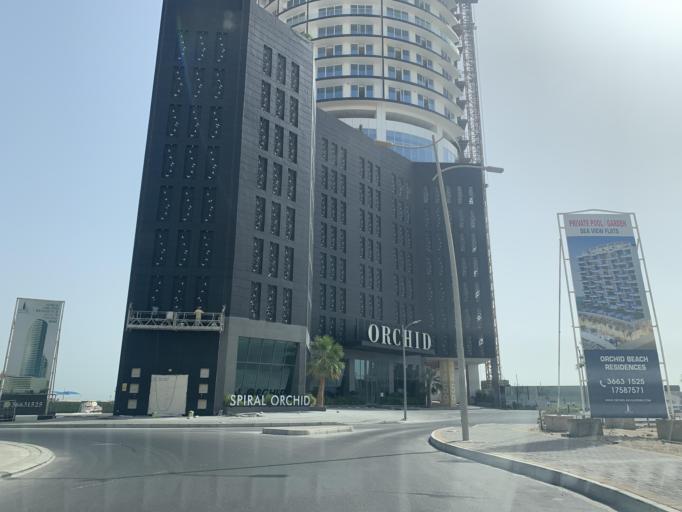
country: BH
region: Manama
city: Jidd Hafs
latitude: 26.2440
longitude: 50.5531
